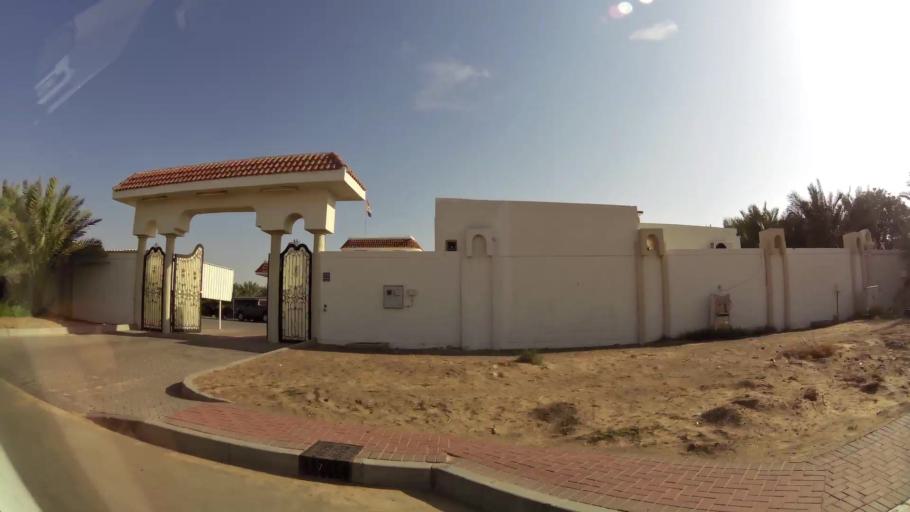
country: AE
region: Abu Dhabi
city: Al Ain
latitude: 24.0337
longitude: 55.8506
